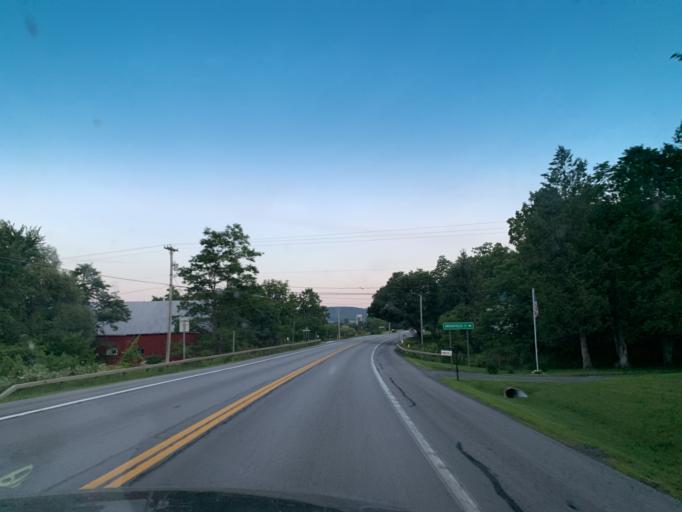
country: US
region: New York
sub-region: Oneida County
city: Waterville
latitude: 42.8217
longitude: -75.2534
